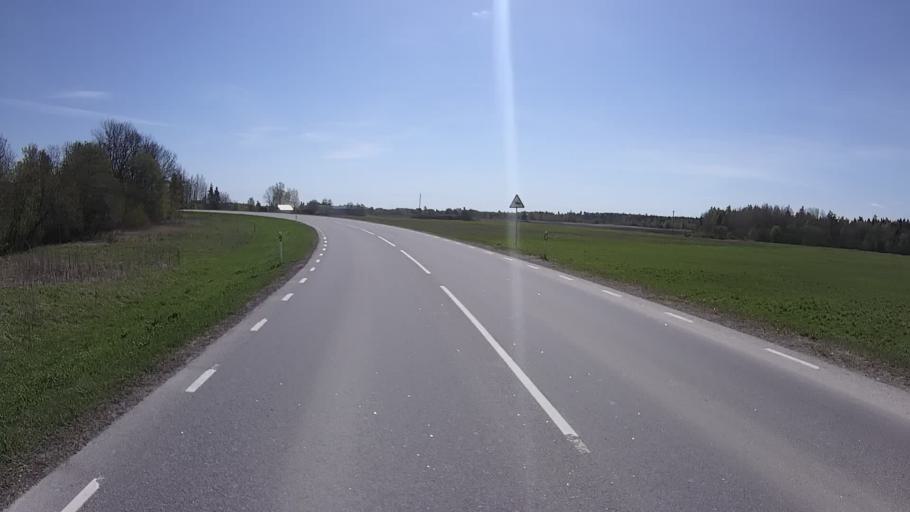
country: EE
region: Harju
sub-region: Keila linn
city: Keila
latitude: 59.3124
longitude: 24.3168
